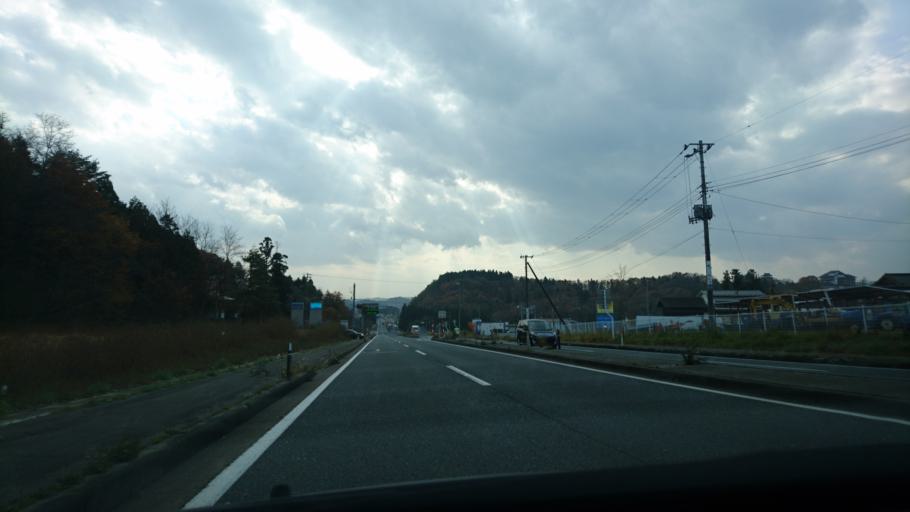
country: JP
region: Iwate
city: Ichinoseki
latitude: 39.0235
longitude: 141.1160
